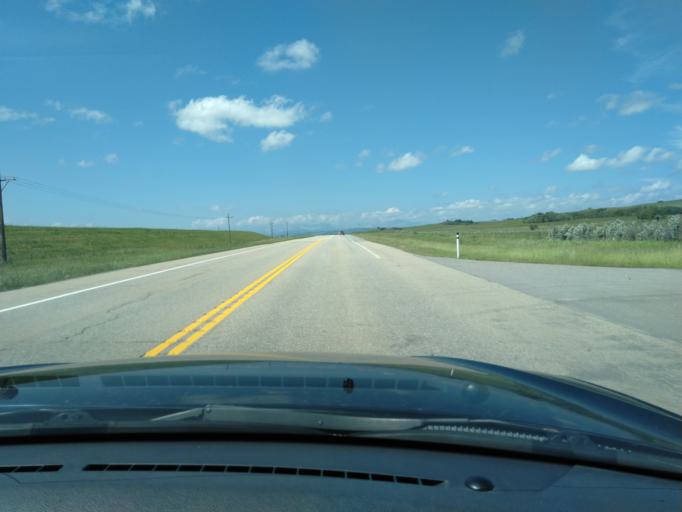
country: CA
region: Alberta
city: Cochrane
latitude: 51.2263
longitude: -114.5919
